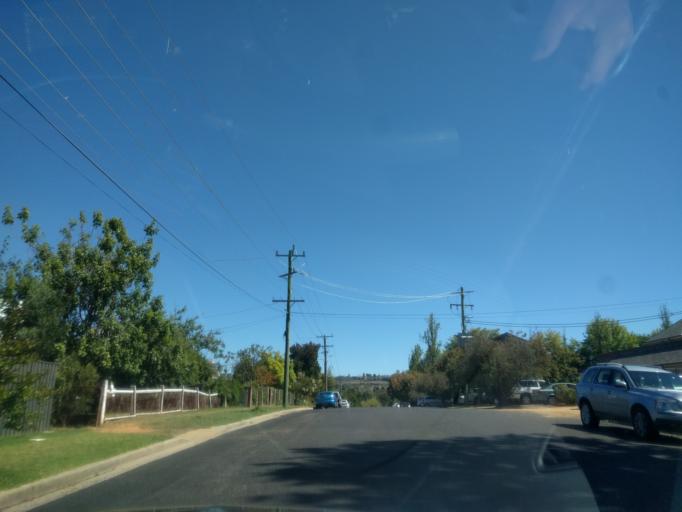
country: AU
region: New South Wales
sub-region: Armidale Dumaresq
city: Armidale
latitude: -30.5230
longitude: 151.6638
